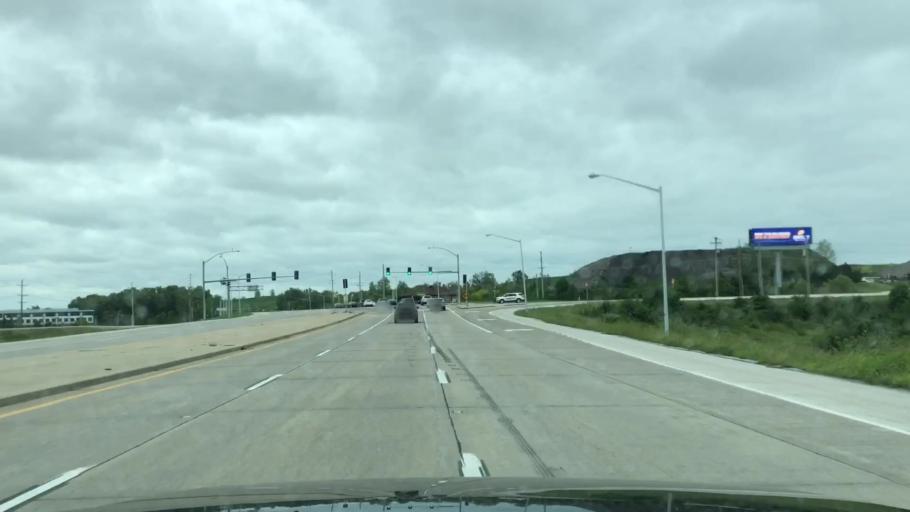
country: US
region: Missouri
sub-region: Saint Charles County
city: Saint Charles
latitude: 38.7417
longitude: -90.4713
